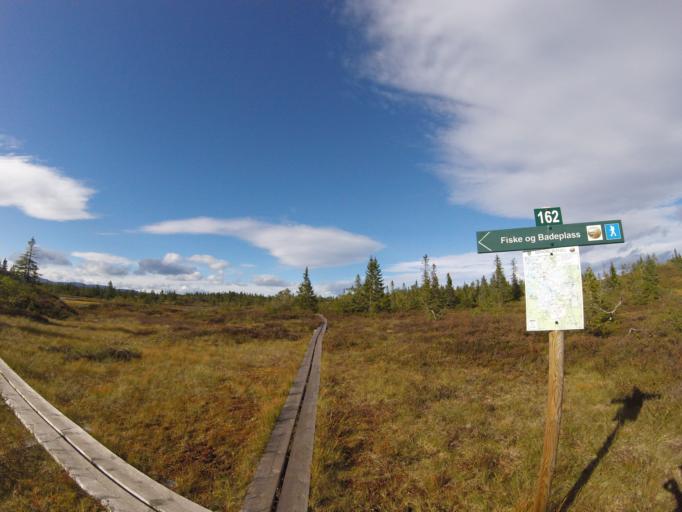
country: NO
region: Buskerud
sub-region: Flesberg
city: Lampeland
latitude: 59.7656
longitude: 9.4120
